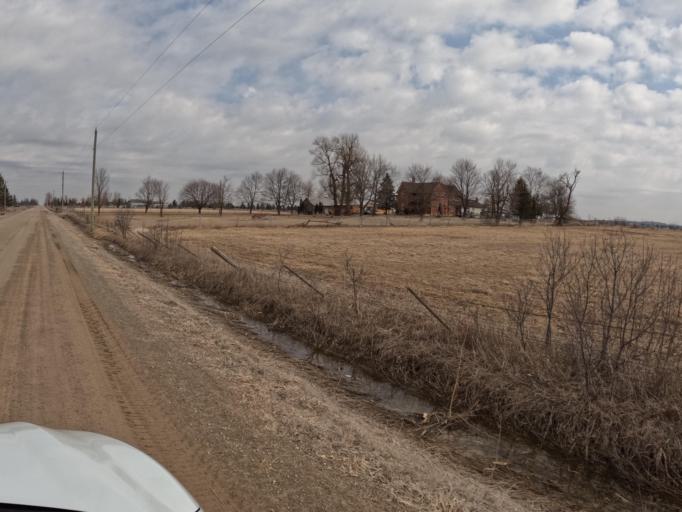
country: CA
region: Ontario
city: Orangeville
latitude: 43.9009
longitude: -80.2132
